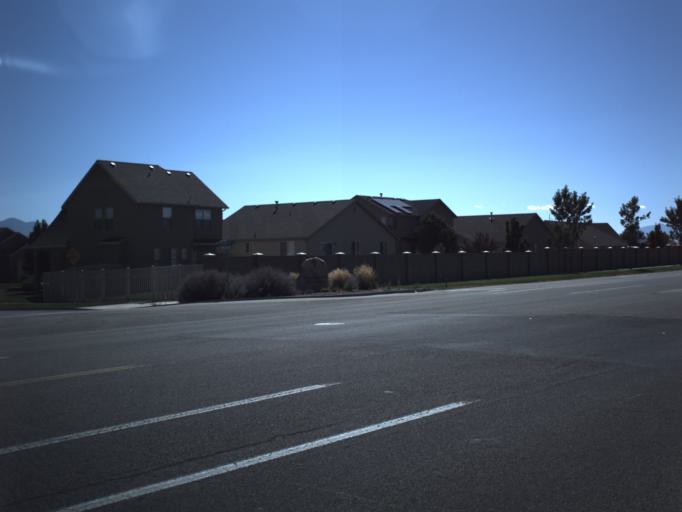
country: US
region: Utah
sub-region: Utah County
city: Saratoga Springs
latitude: 40.3757
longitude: -111.9165
